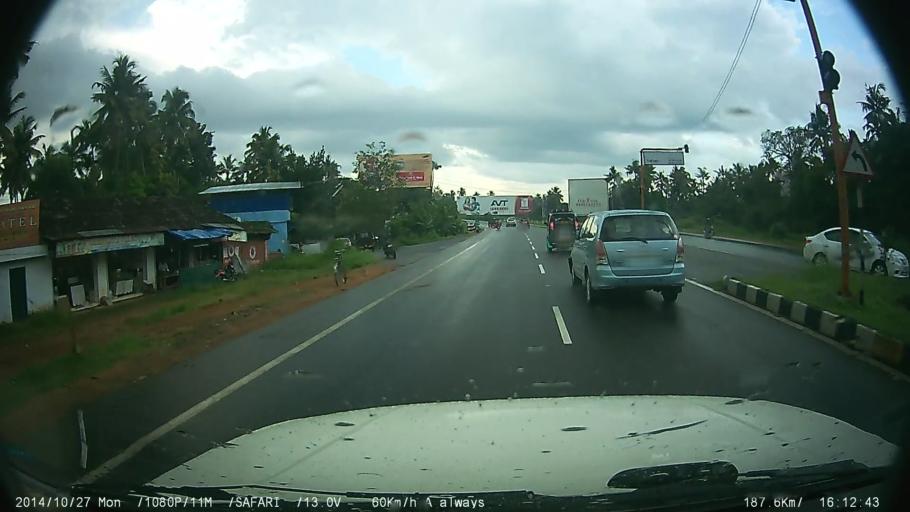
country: IN
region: Kerala
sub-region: Thrissur District
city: Irinjalakuda
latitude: 10.4081
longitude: 76.2744
